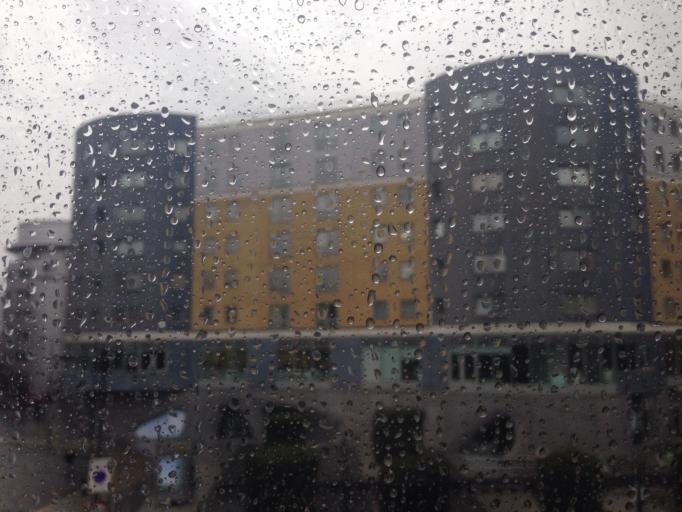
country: GB
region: England
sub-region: Greater London
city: Chelsea
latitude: 51.4749
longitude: -0.1827
